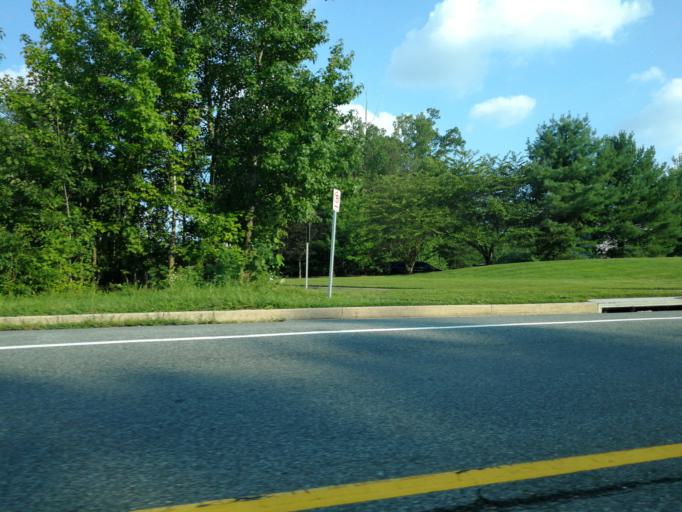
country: US
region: Maryland
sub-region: Harford County
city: Riverside
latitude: 39.4825
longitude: -76.2437
